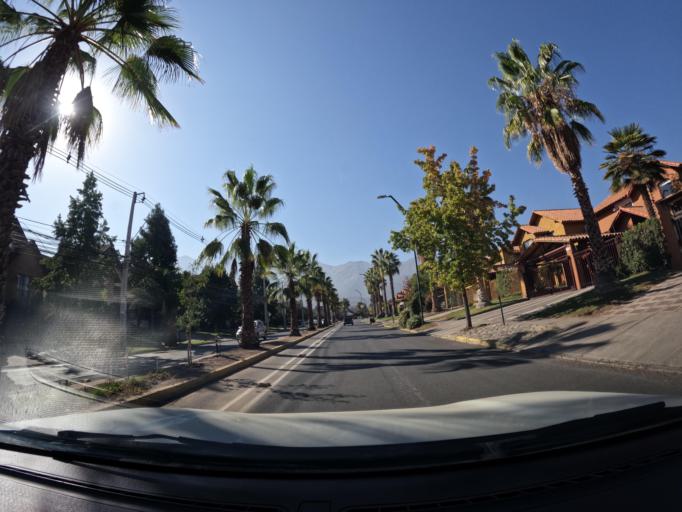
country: CL
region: Santiago Metropolitan
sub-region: Provincia de Santiago
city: Villa Presidente Frei, Nunoa, Santiago, Chile
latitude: -33.4820
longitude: -70.5492
